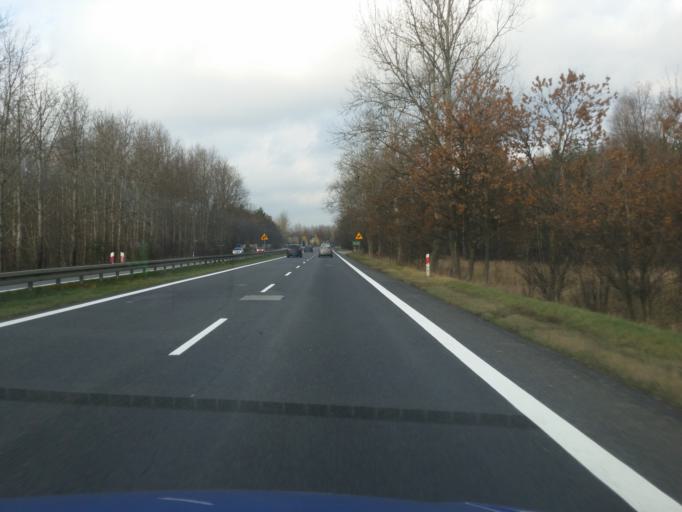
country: PL
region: Silesian Voivodeship
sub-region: Powiat bedzinski
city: Siewierz
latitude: 50.4822
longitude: 19.2221
